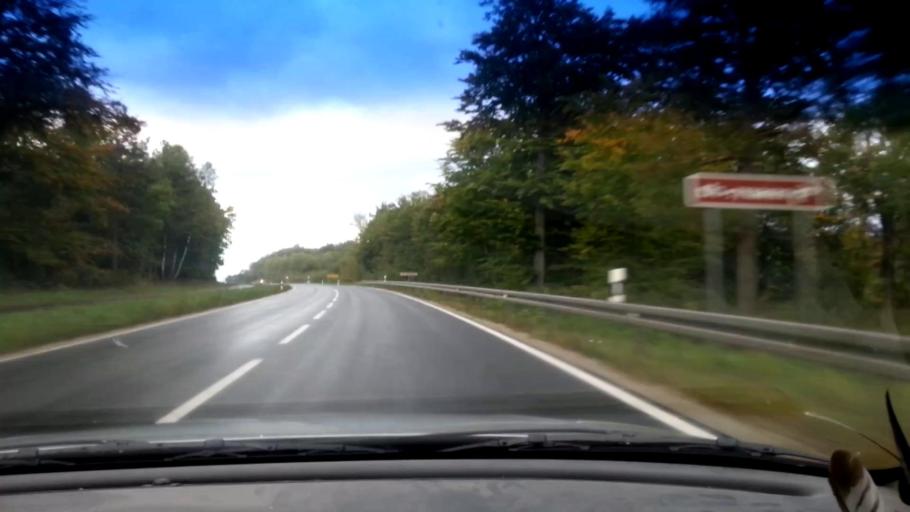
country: DE
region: Bavaria
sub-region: Upper Franconia
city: Burgebrach
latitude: 49.8066
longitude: 10.7310
